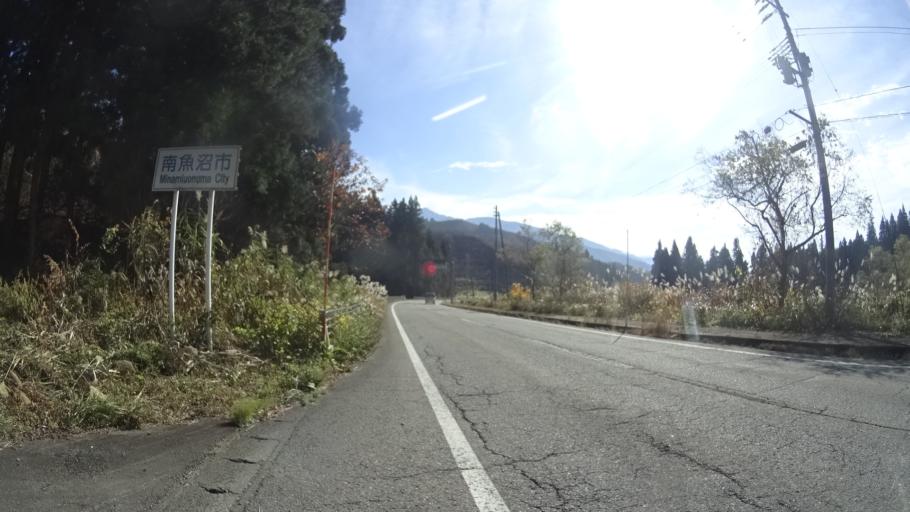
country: JP
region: Niigata
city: Muikamachi
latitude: 37.1907
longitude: 138.9811
